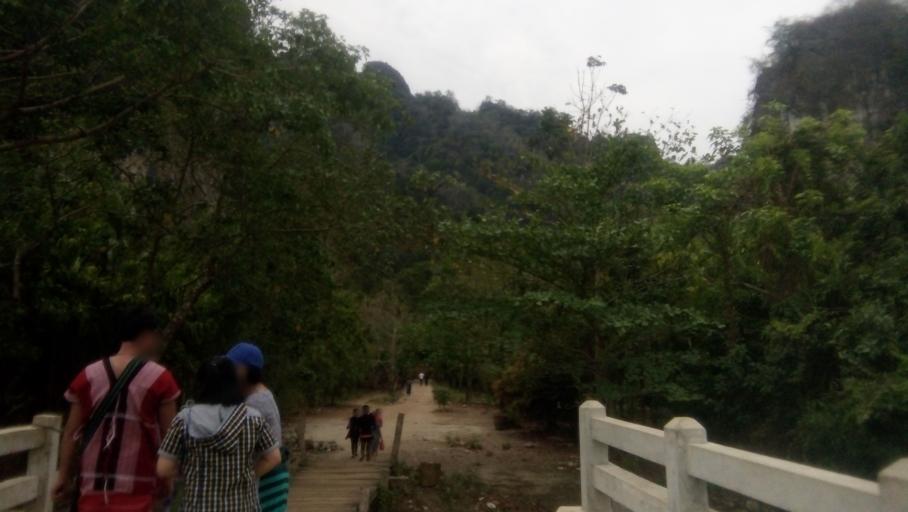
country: MM
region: Kayin
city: Hpa-an
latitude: 16.9108
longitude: 97.7486
